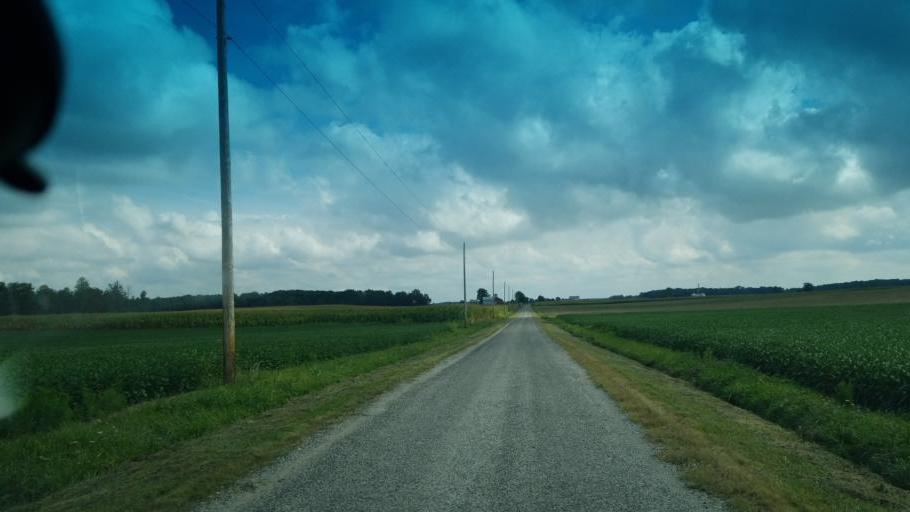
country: US
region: Ohio
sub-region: Crawford County
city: Bucyrus
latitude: 40.9793
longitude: -82.9504
